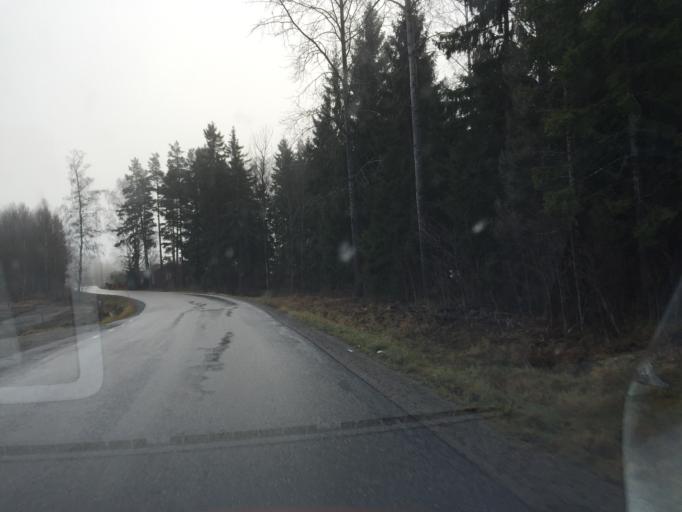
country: SE
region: Stockholm
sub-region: Nynashamns Kommun
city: Osmo
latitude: 59.0735
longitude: 17.8781
